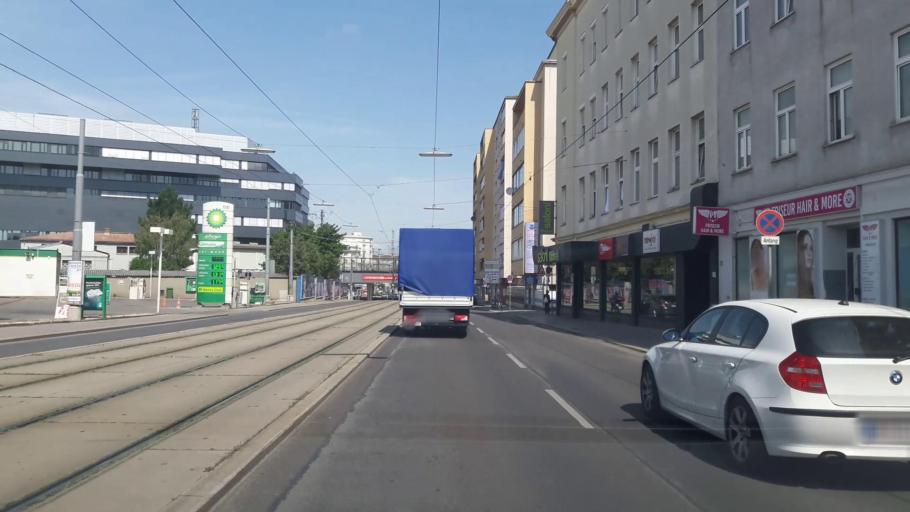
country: AT
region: Vienna
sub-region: Wien Stadt
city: Vienna
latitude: 48.1831
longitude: 16.3737
